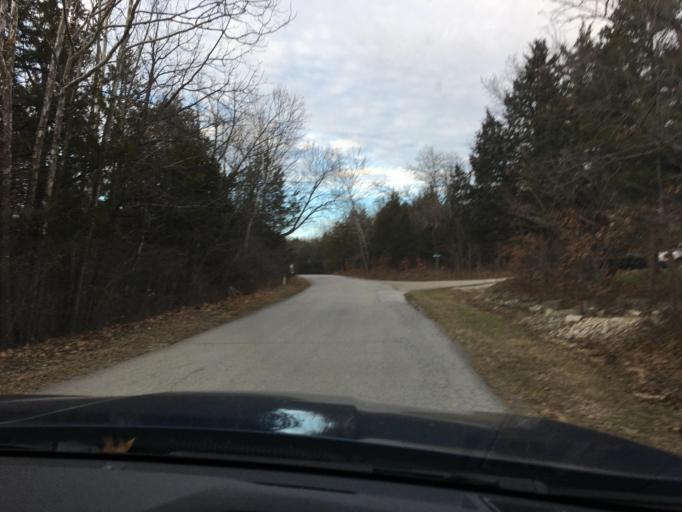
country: US
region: Missouri
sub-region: Jefferson County
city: De Soto
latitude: 38.0928
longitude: -90.5661
